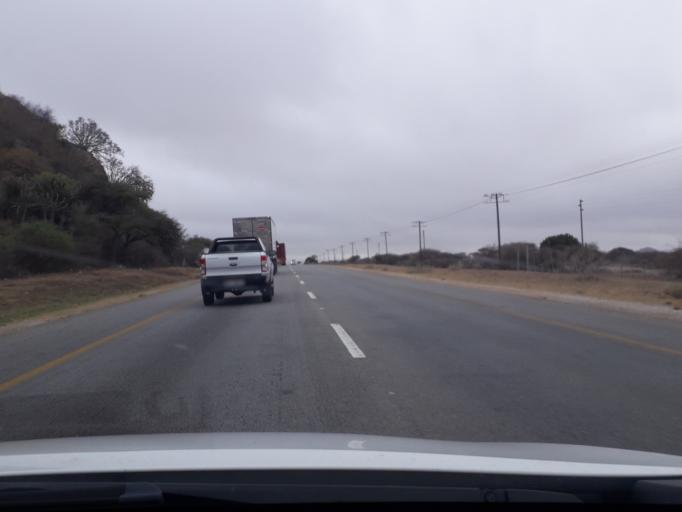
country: ZA
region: Limpopo
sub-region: Capricorn District Municipality
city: Mankoeng
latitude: -23.5259
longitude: 29.7061
